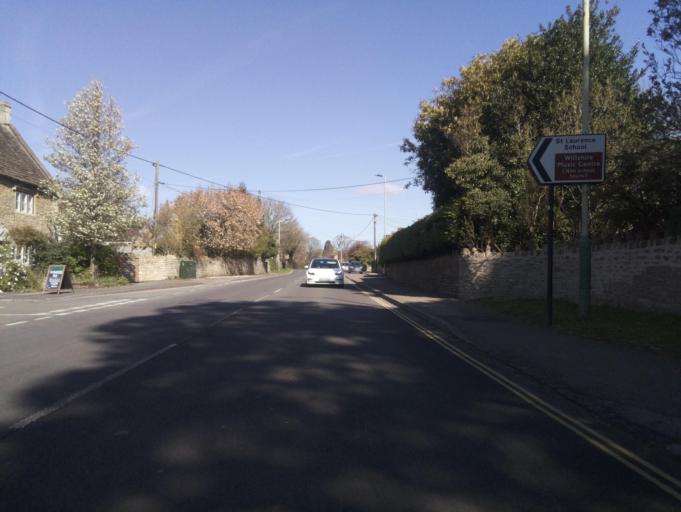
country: GB
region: England
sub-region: Wiltshire
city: Bradford-on-Avon
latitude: 51.3532
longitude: -2.2525
